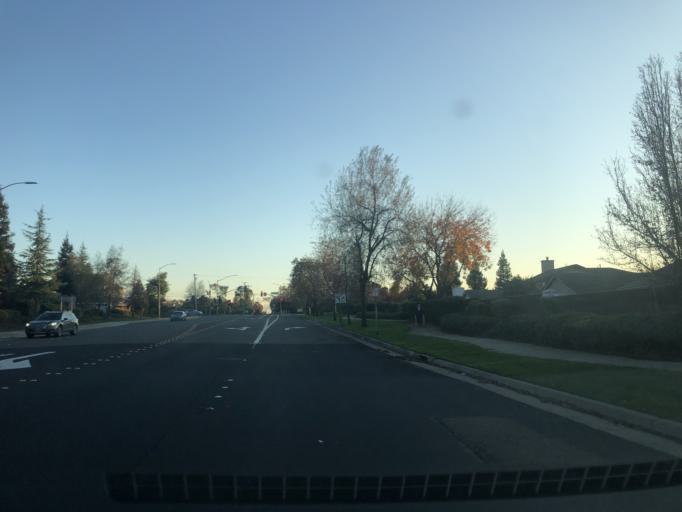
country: US
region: California
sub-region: Sacramento County
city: Antelope
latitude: 38.7536
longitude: -121.3371
